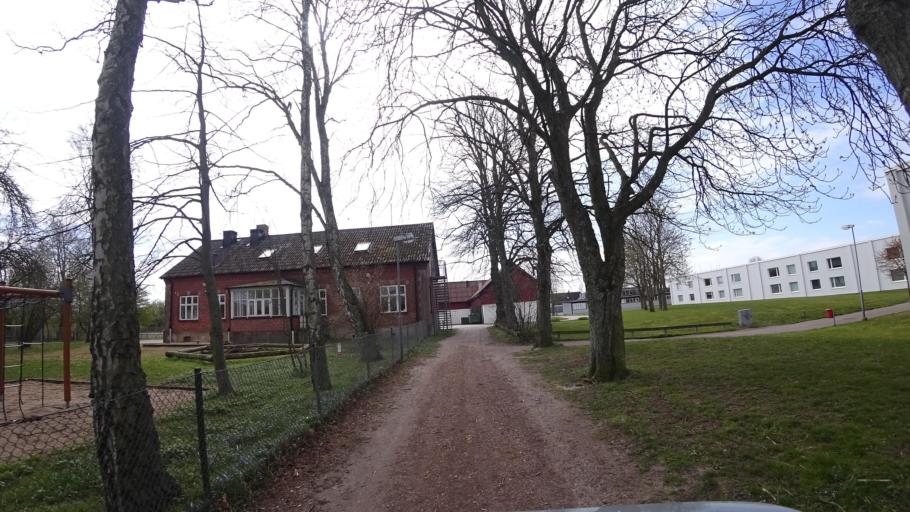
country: SE
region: Skane
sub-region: Staffanstorps Kommun
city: Staffanstorp
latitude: 55.6398
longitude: 13.2020
